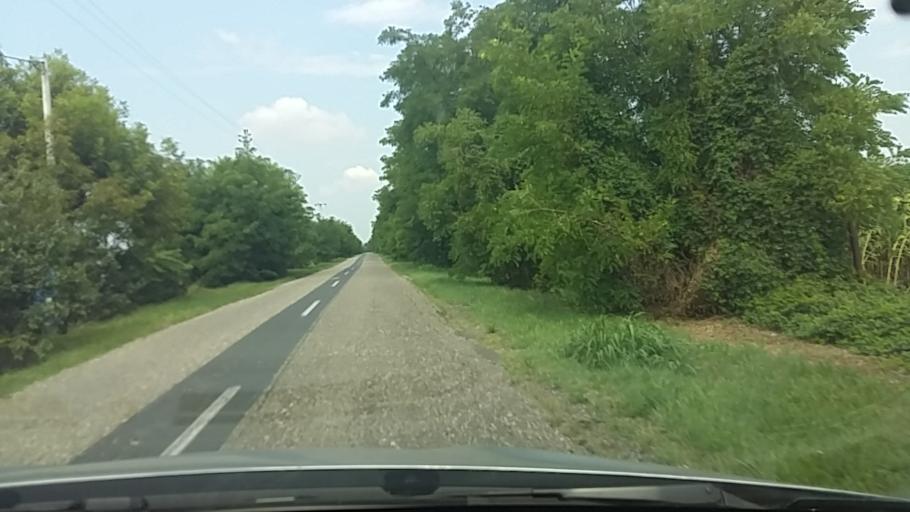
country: HU
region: Pest
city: Rackeve
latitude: 47.1943
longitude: 18.9258
